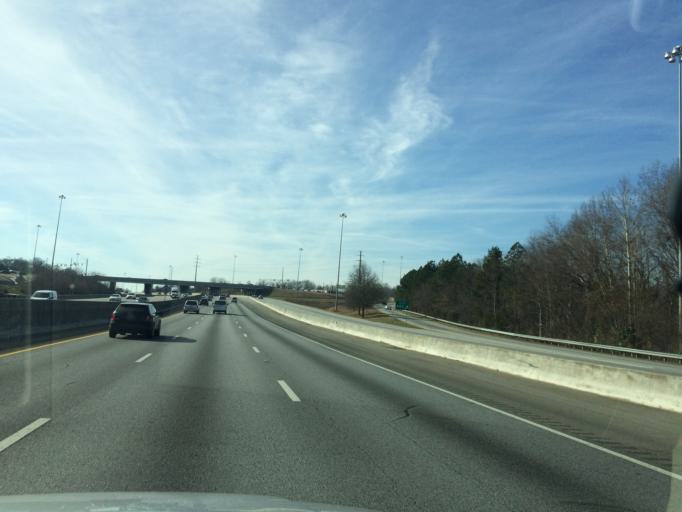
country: US
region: South Carolina
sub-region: Greenville County
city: Greenville
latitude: 34.8012
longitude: -82.3649
